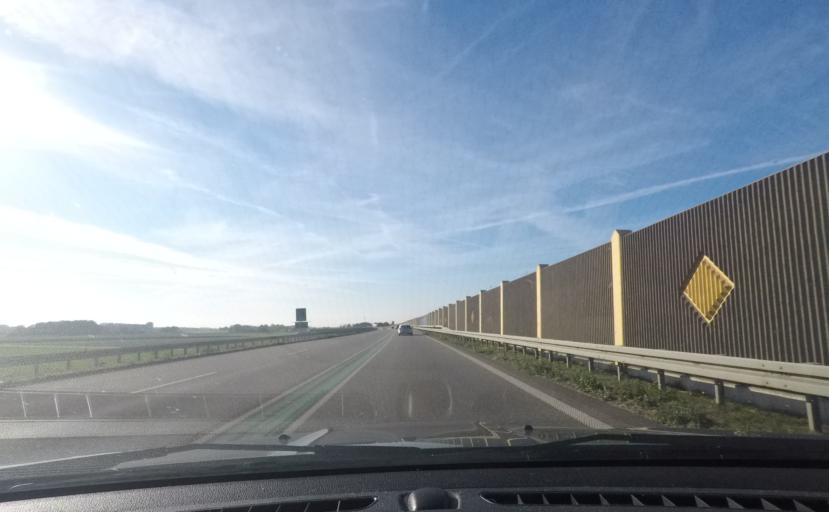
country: DE
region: North Rhine-Westphalia
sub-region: Regierungsbezirk Munster
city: Borken
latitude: 51.8299
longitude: 6.8428
